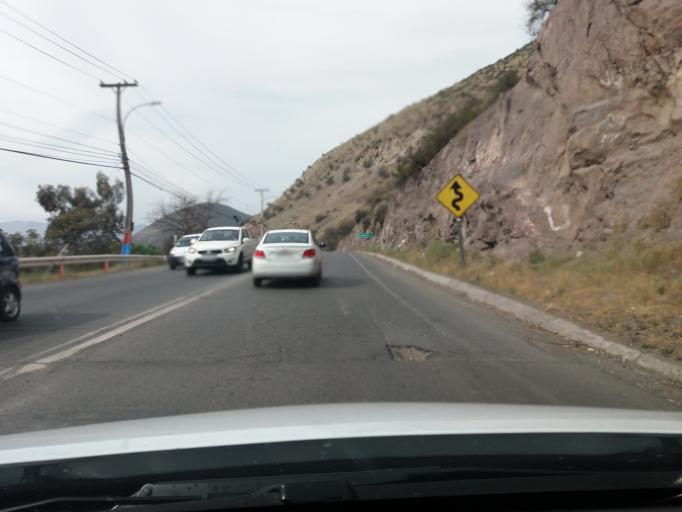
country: CL
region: Valparaiso
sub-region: Provincia de San Felipe
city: San Felipe
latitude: -32.7582
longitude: -70.7367
